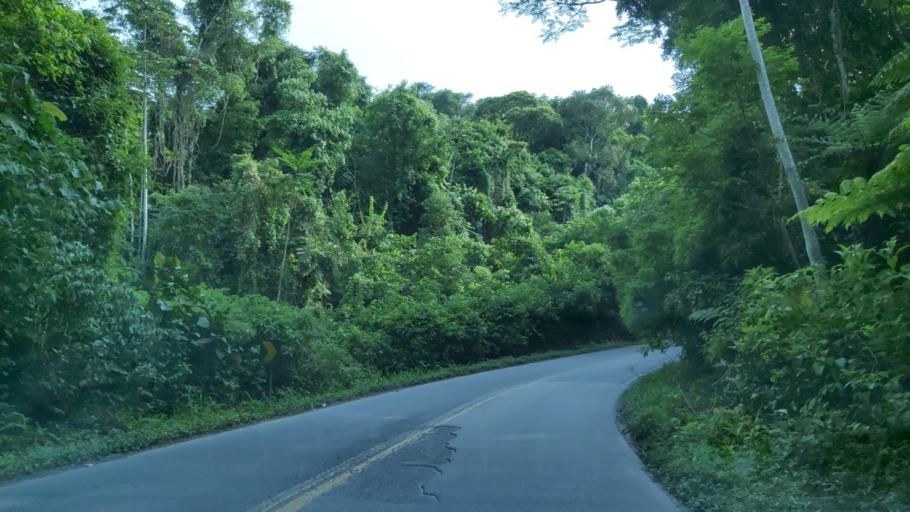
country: BR
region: Sao Paulo
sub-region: Juquia
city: Juquia
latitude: -24.0995
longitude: -47.6241
